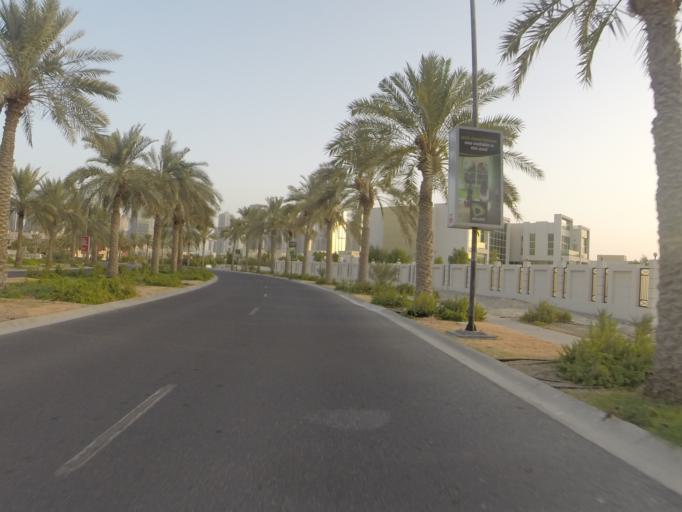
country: AE
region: Dubai
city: Dubai
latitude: 25.0662
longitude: 55.1506
